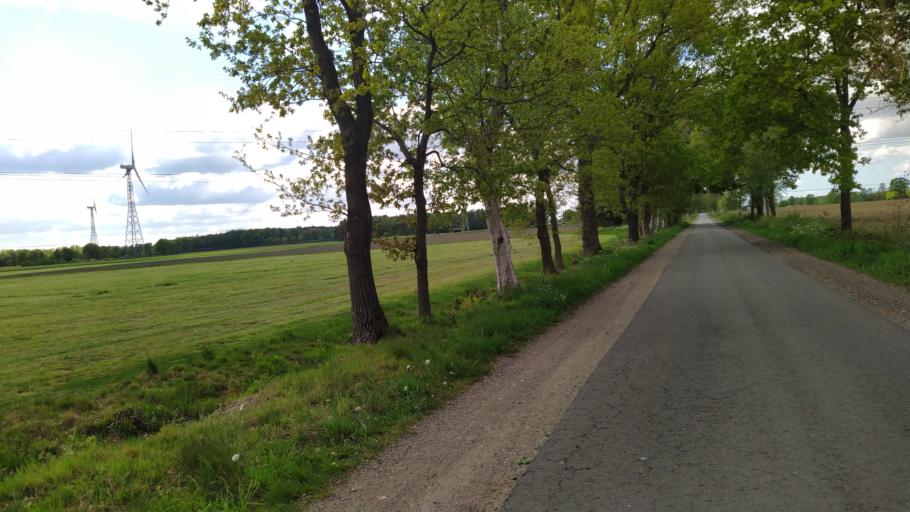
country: DE
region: Lower Saxony
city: Brest
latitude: 53.4415
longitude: 9.4027
